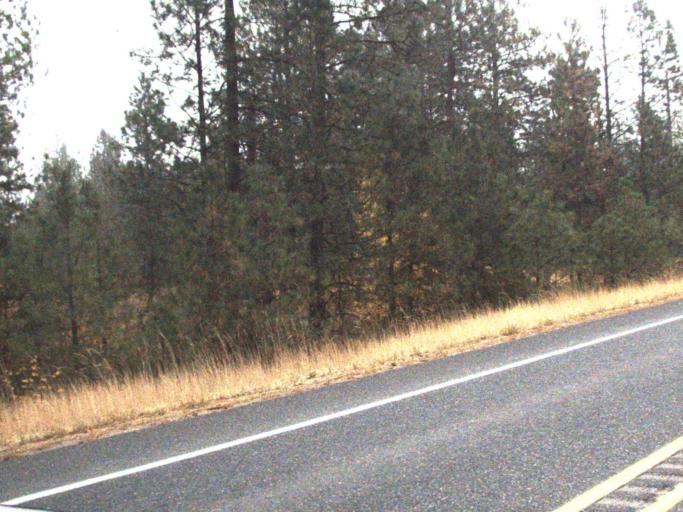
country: US
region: Washington
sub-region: Stevens County
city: Kettle Falls
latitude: 48.6127
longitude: -118.0966
